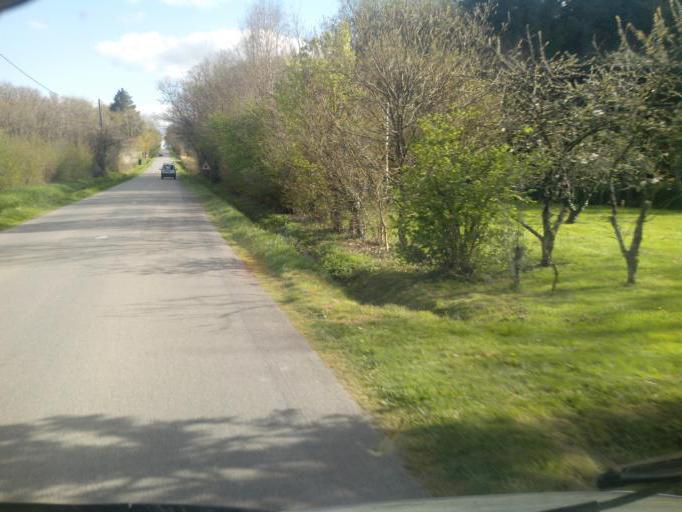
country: FR
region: Brittany
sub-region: Departement d'Ille-et-Vilaine
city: Grand-Fougeray
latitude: 47.7501
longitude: -1.7465
